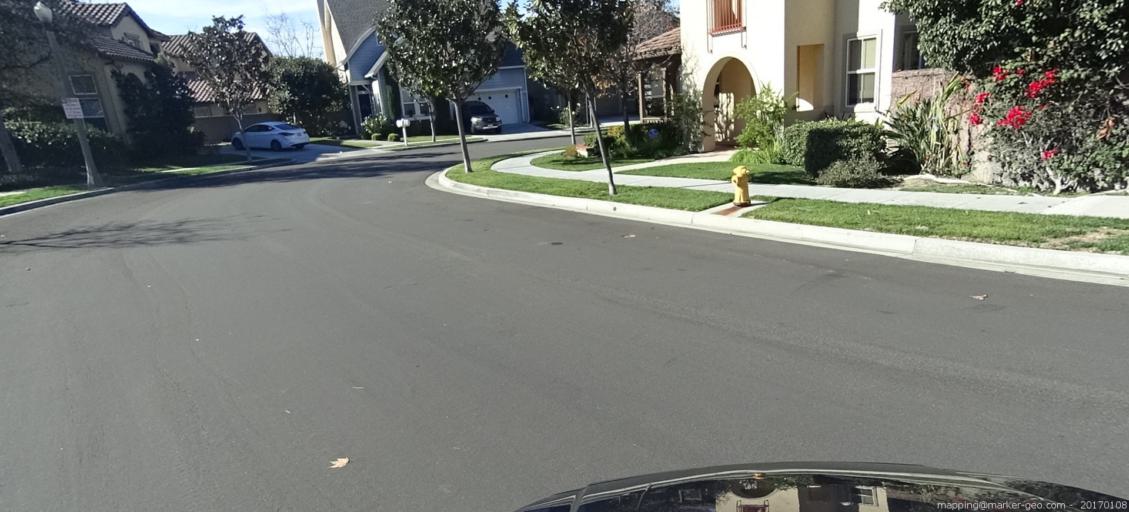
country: US
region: California
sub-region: Orange County
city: Ladera Ranch
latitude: 33.5682
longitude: -117.6413
